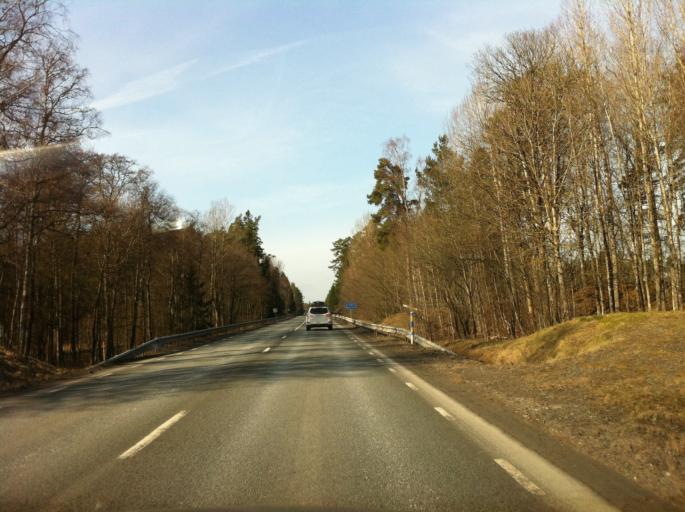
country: SE
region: Joenkoeping
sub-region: Jonkopings Kommun
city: Bankeryd
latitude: 57.8416
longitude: 14.0551
